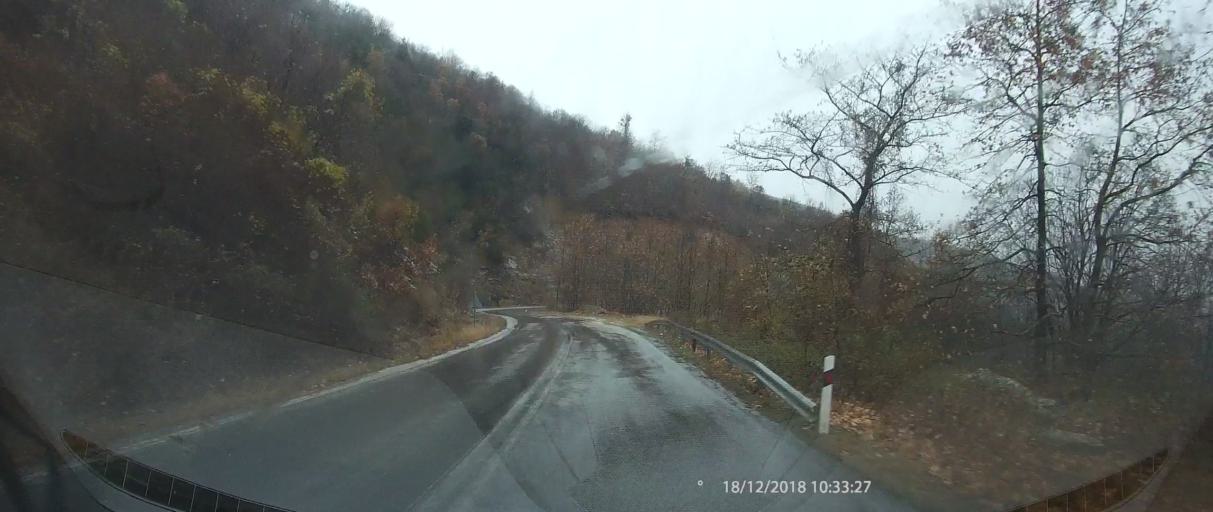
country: GR
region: Central Macedonia
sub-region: Nomos Pierias
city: Kato Milia
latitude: 40.1980
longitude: 22.3009
